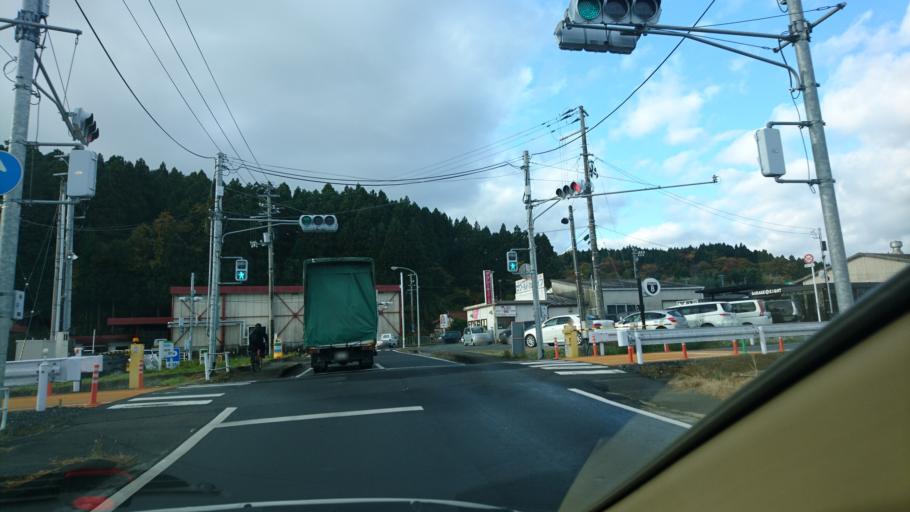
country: JP
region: Iwate
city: Ofunato
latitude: 38.9014
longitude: 141.5547
